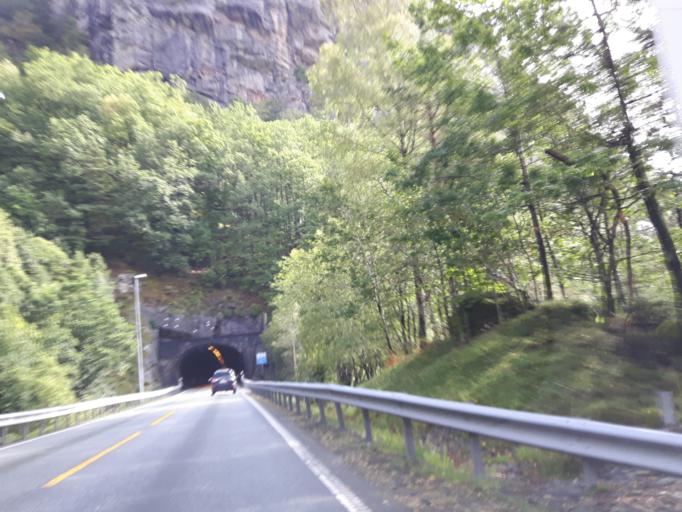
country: NO
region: Vest-Agder
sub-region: Flekkefjord
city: Flekkefjord
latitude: 58.3558
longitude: 6.6511
